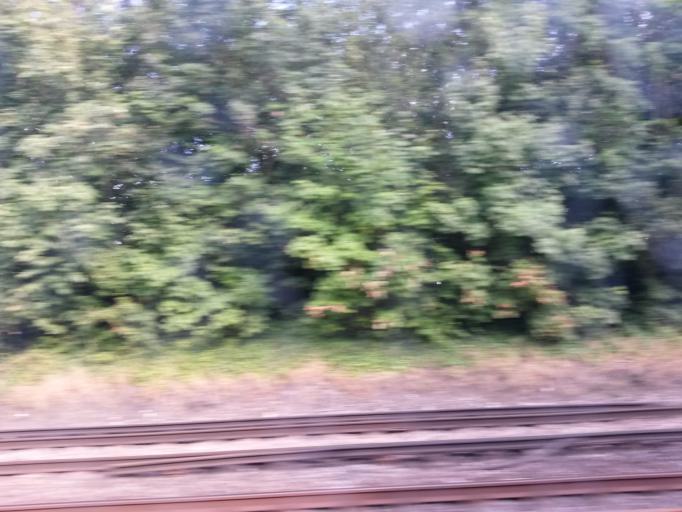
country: GB
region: England
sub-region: Greater London
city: Catford
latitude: 51.4428
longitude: -0.0512
